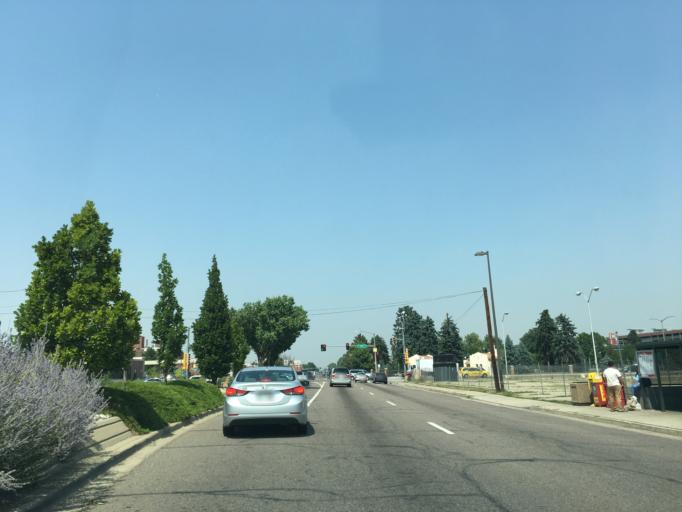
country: US
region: Colorado
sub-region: Adams County
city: Aurora
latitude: 39.7391
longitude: -104.8470
